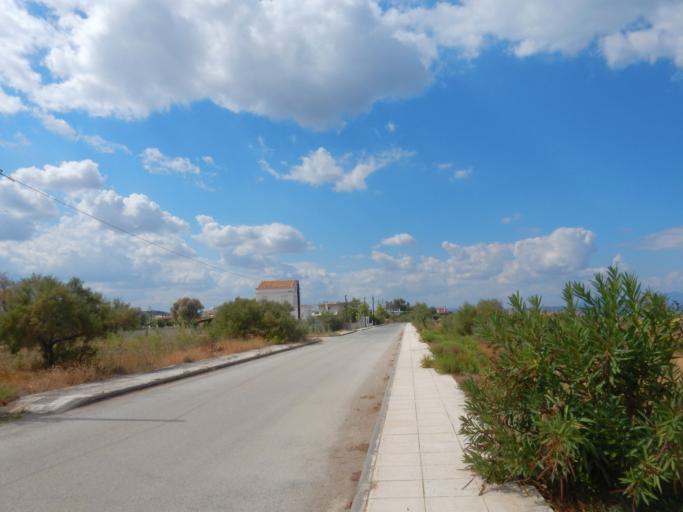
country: GR
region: Attica
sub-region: Nomarchia Anatolikis Attikis
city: Skala Oropou
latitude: 38.3363
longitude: 23.7623
